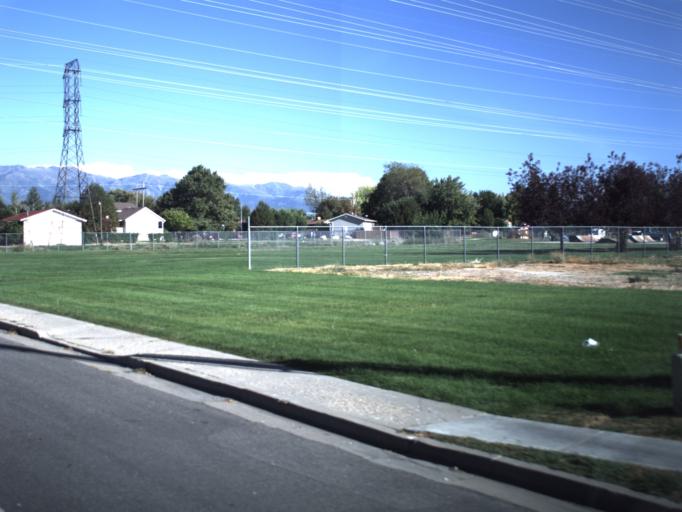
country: US
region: Utah
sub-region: Davis County
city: Clinton
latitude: 41.1398
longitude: -112.0591
